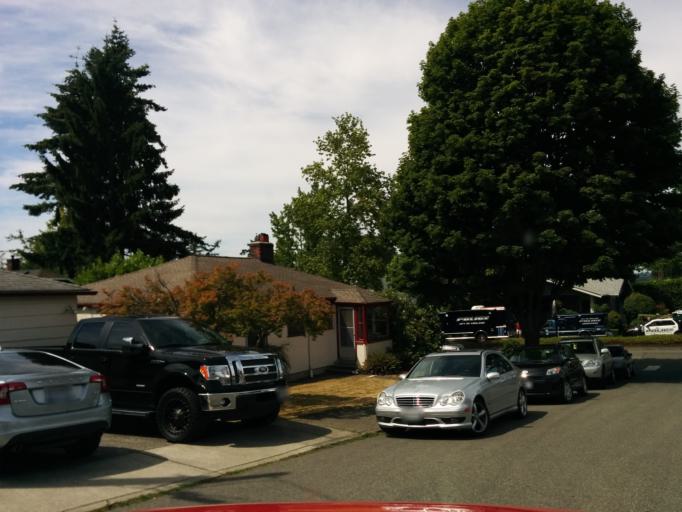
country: US
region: Washington
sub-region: King County
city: Kirkland
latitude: 47.6788
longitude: -122.2089
